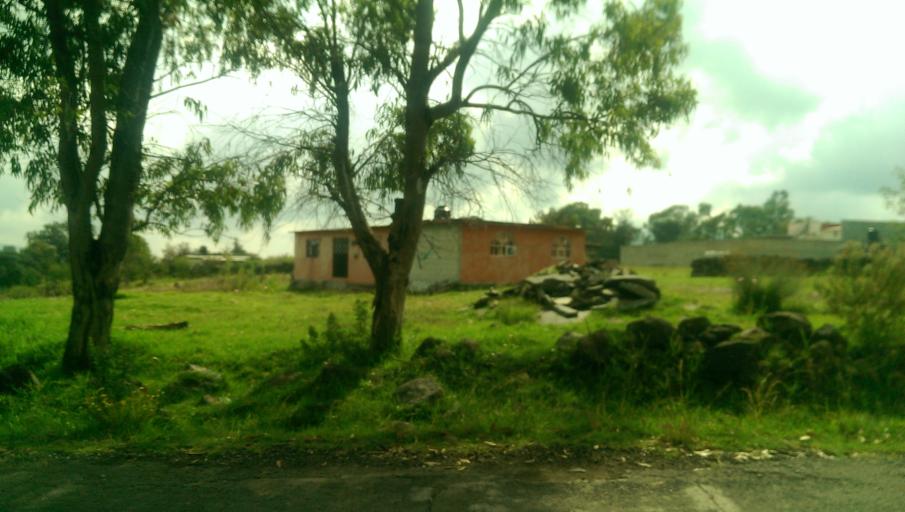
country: MX
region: Mexico
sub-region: Jilotepec
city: Jilotepec de Molina Enriquez
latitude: 19.9603
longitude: -99.4876
